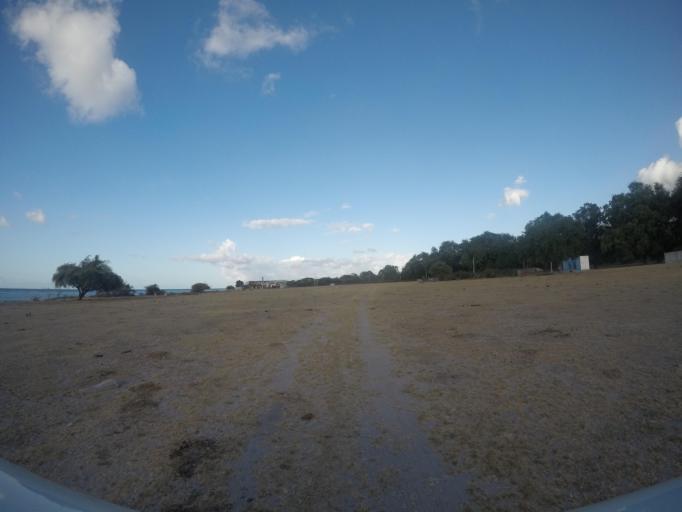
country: TL
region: Lautem
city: Lospalos
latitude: -8.3245
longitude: 126.9923
